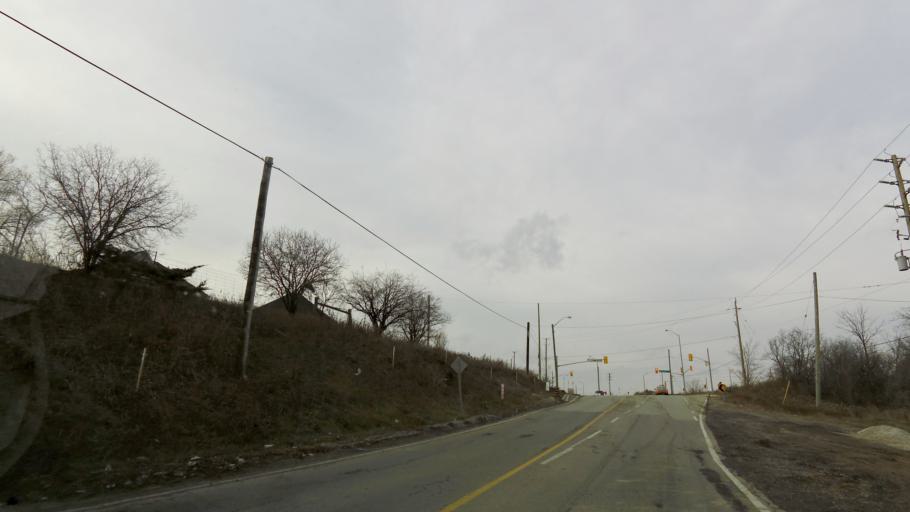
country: CA
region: Ontario
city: Etobicoke
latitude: 43.7645
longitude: -79.6526
